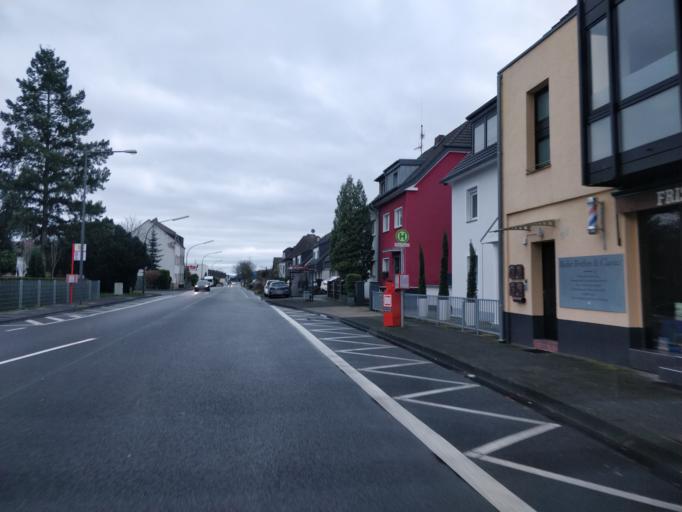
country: DE
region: North Rhine-Westphalia
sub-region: Regierungsbezirk Koln
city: Wahn-Heide
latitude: 50.8527
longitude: 7.0896
